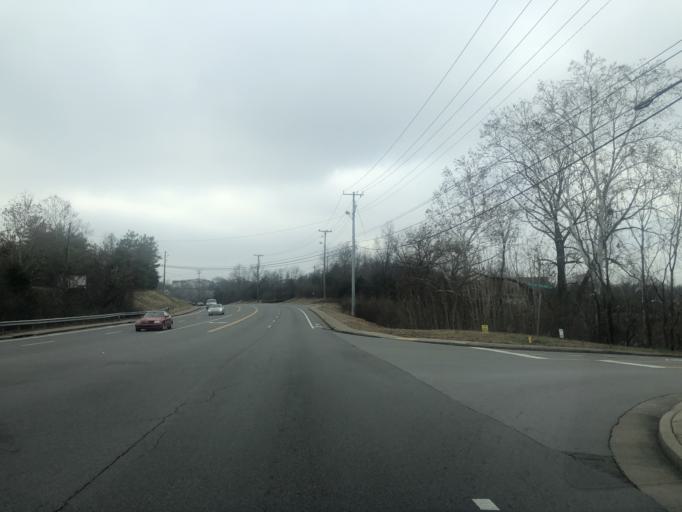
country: US
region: Tennessee
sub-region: Rutherford County
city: La Vergne
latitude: 36.0608
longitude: -86.6397
